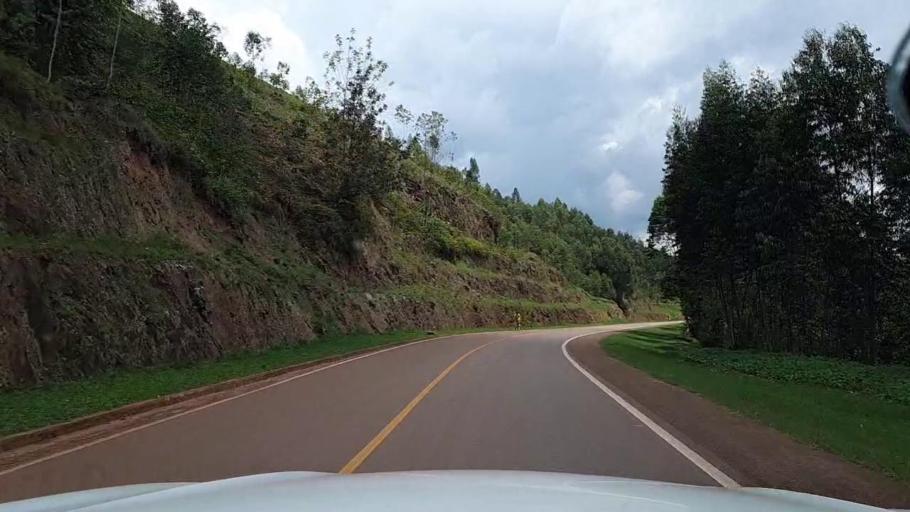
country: RW
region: Kigali
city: Kigali
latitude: -1.8149
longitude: 30.1189
